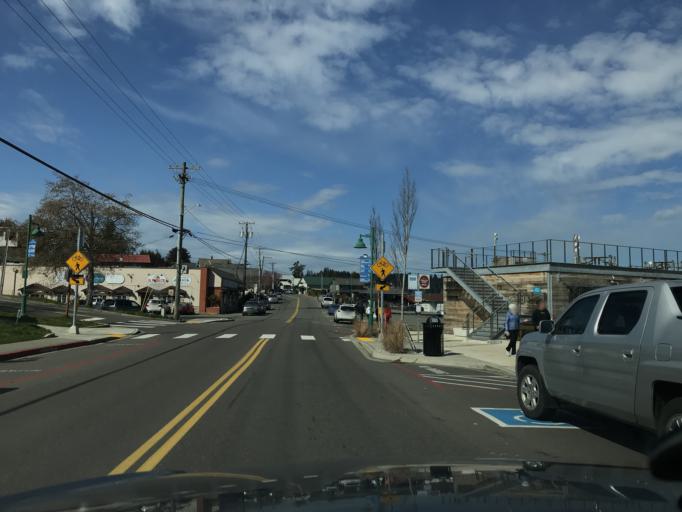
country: US
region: Washington
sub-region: Pierce County
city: Gig Harbor
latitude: 47.3305
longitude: -122.5819
